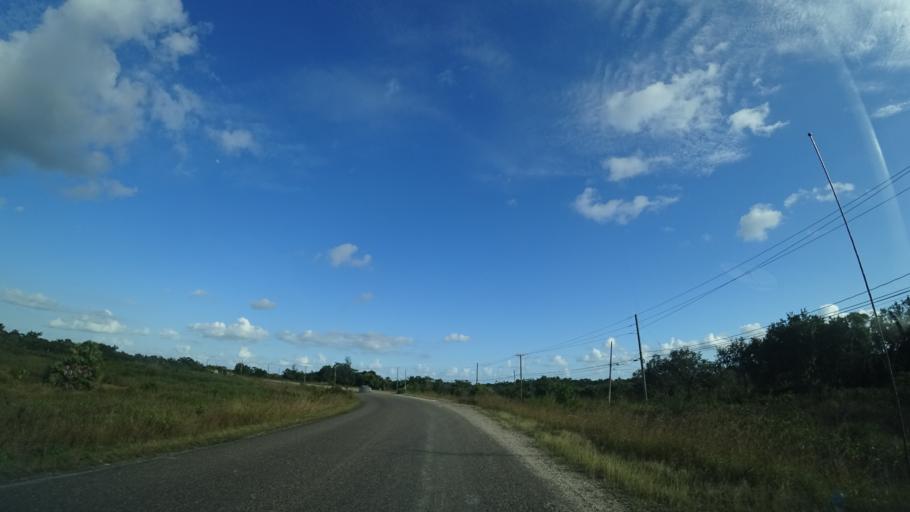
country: BZ
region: Belize
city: Belize City
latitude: 17.5799
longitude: -88.3719
